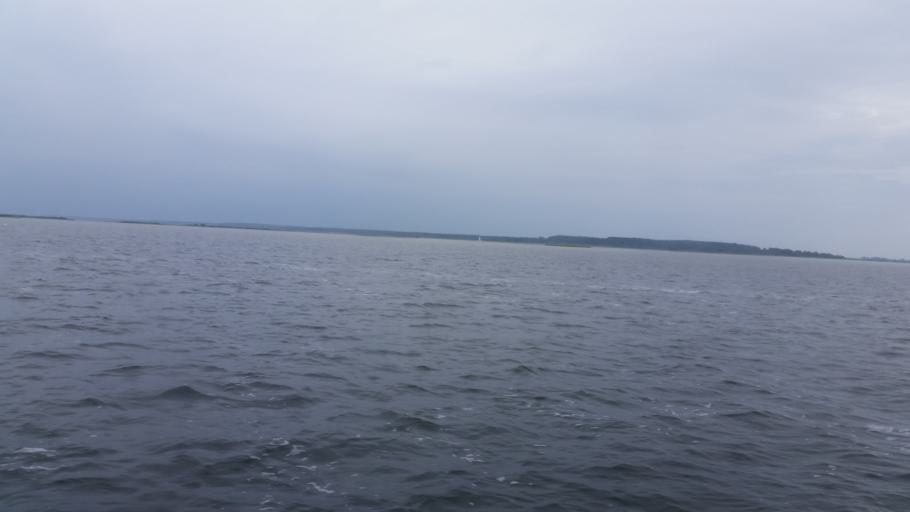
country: DE
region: Mecklenburg-Vorpommern
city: Hiddensee
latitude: 54.5675
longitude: 13.1314
